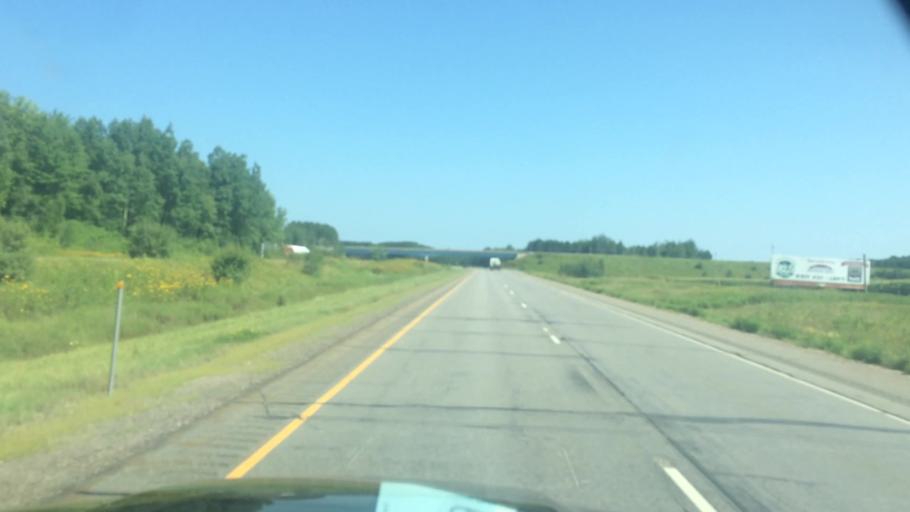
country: US
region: Wisconsin
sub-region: Lincoln County
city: Merrill
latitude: 45.1891
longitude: -89.6461
